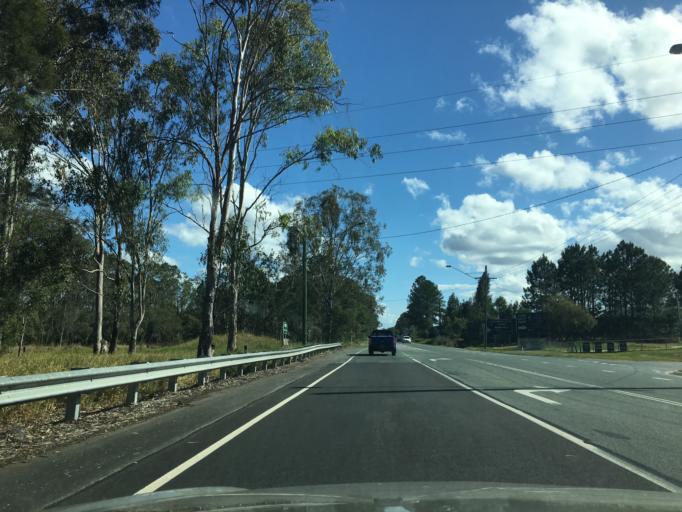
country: AU
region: Queensland
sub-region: Logan
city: Chambers Flat
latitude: -27.7707
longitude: 153.1062
